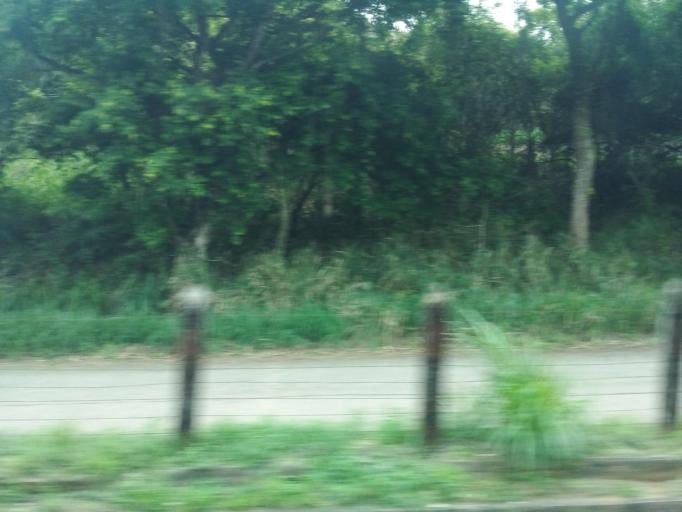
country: BR
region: Minas Gerais
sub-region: Nova Era
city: Nova Era
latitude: -19.7266
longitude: -42.9942
